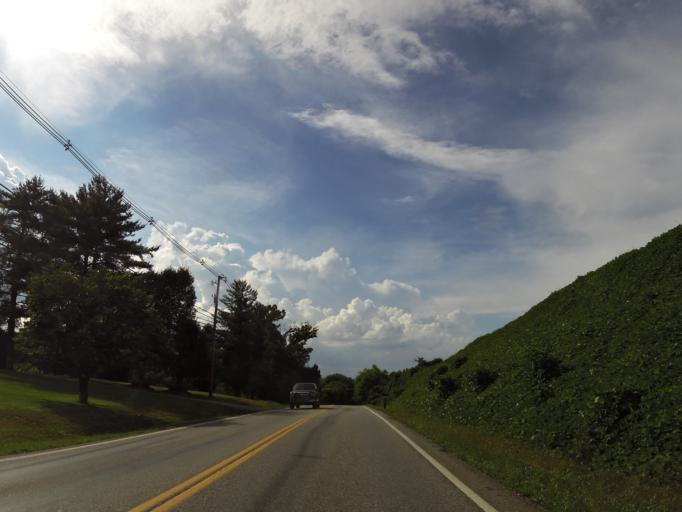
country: US
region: Tennessee
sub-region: Blount County
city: Louisville
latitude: 35.7997
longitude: -84.0186
